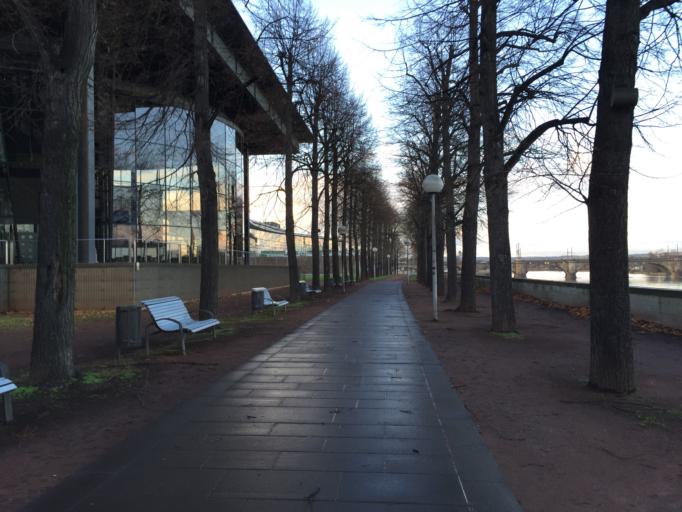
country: DE
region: Saxony
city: Dresden
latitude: 51.0570
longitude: 13.7339
